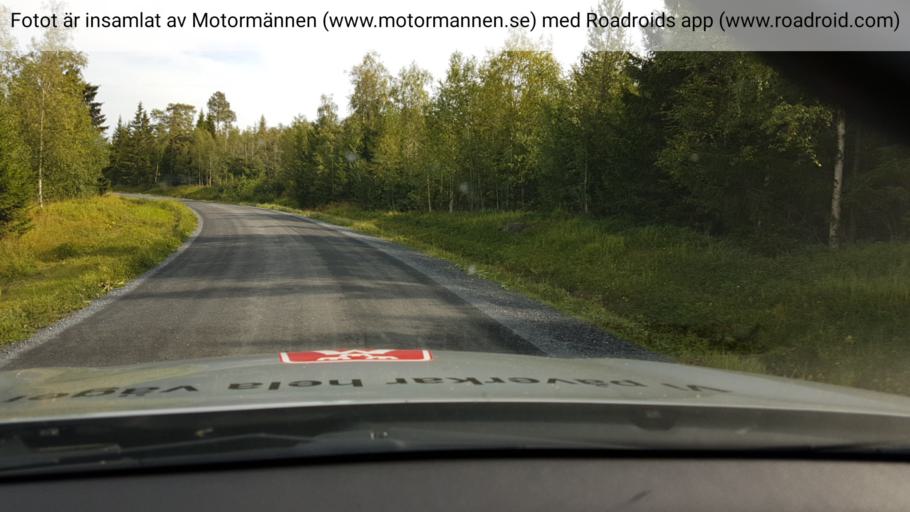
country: SE
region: Jaemtland
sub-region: Krokoms Kommun
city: Valla
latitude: 63.3655
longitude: 13.9055
